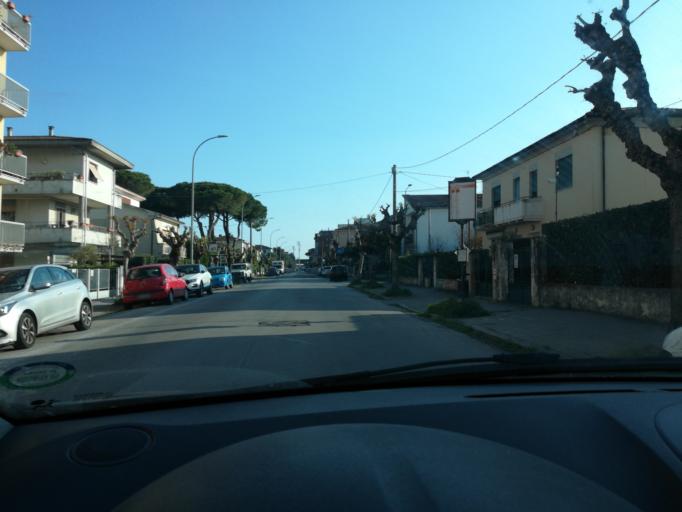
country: IT
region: Tuscany
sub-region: Province of Pisa
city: Pisa
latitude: 43.7331
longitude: 10.4005
